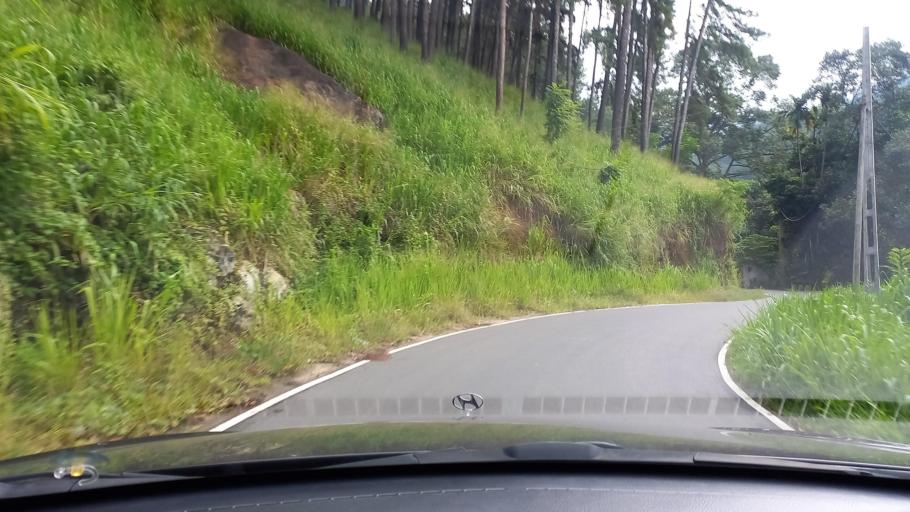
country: LK
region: Central
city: Gampola
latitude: 7.2117
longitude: 80.6177
